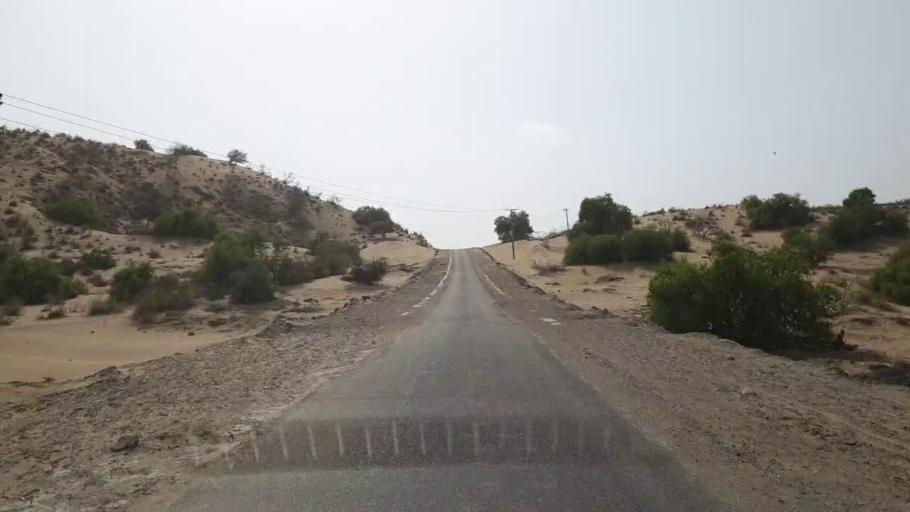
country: PK
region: Sindh
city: Mithi
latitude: 24.6212
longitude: 69.9133
